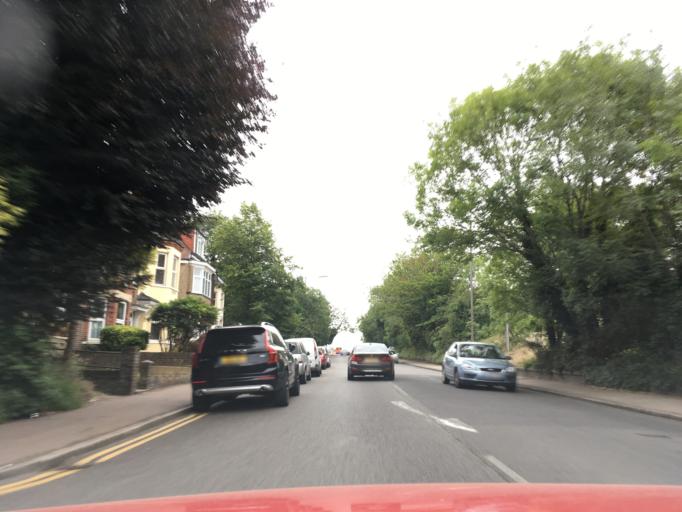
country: GB
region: England
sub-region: Central Bedfordshire
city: Dunstable
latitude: 51.8806
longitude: -0.5127
